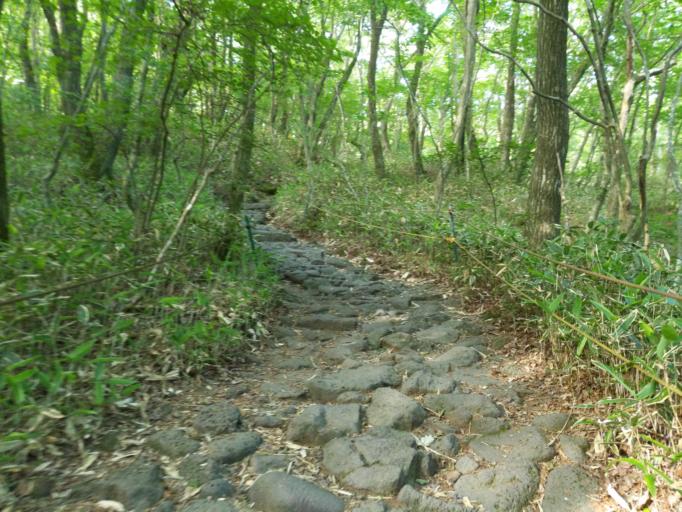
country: KR
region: Jeju-do
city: Jeju-si
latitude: 33.4181
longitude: 126.5482
